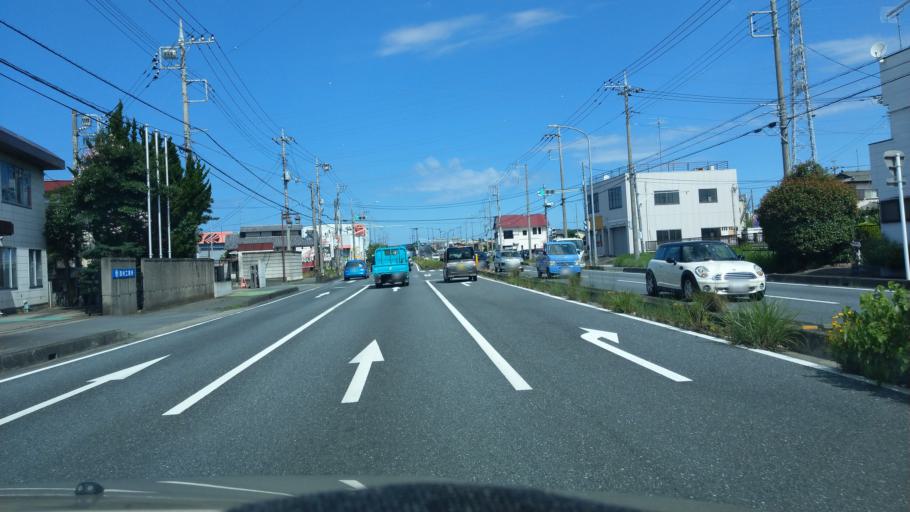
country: JP
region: Saitama
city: Sakado
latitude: 36.0197
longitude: 139.4251
